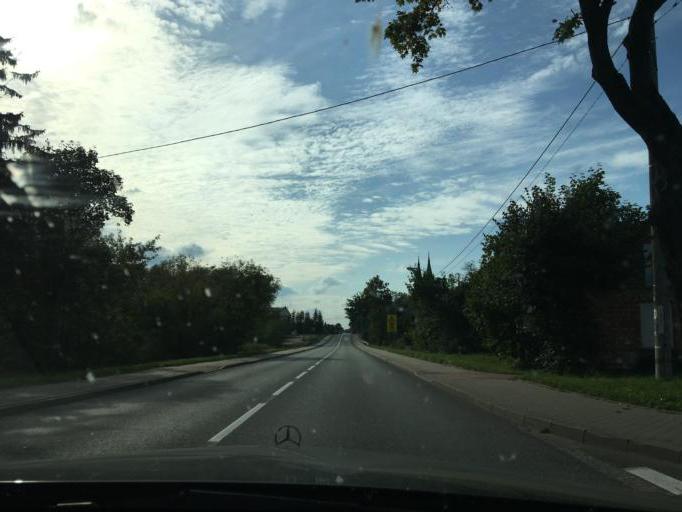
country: PL
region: Podlasie
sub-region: Powiat grajewski
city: Rajgrod
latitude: 53.7310
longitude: 22.7045
